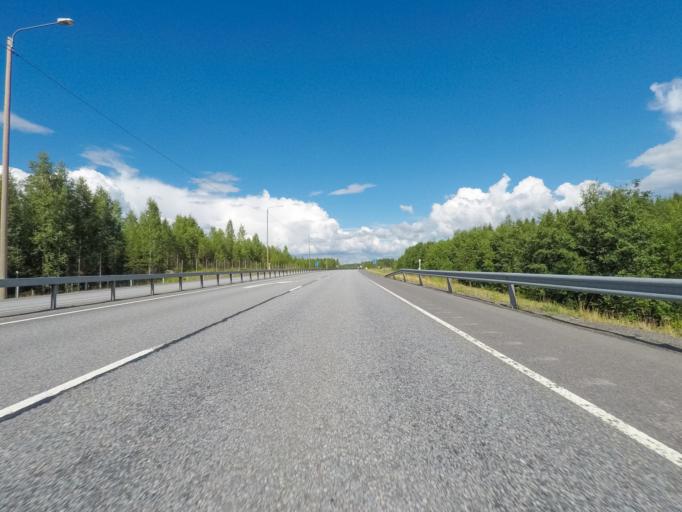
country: FI
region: Southern Savonia
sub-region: Mikkeli
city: Maentyharju
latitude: 61.5376
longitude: 26.8868
